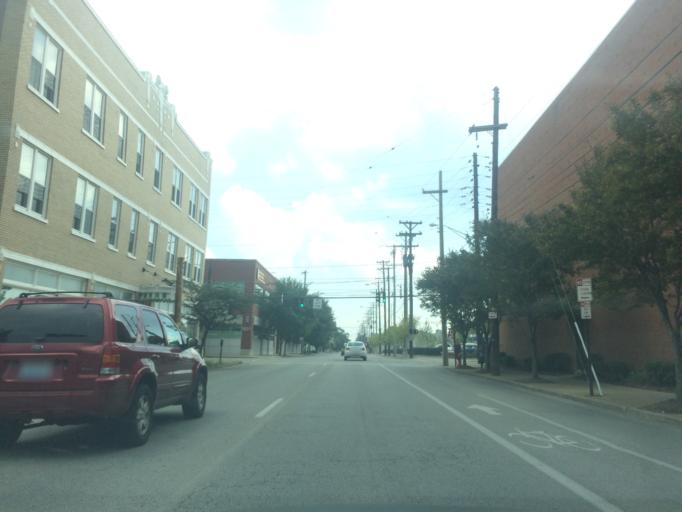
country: US
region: Kentucky
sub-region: Jefferson County
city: Louisville
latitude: 38.2422
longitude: -85.7574
